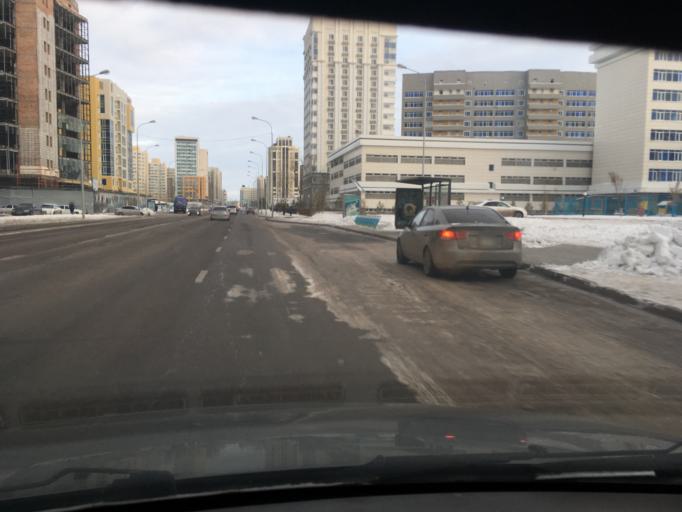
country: KZ
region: Astana Qalasy
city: Astana
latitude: 51.1171
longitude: 71.4209
